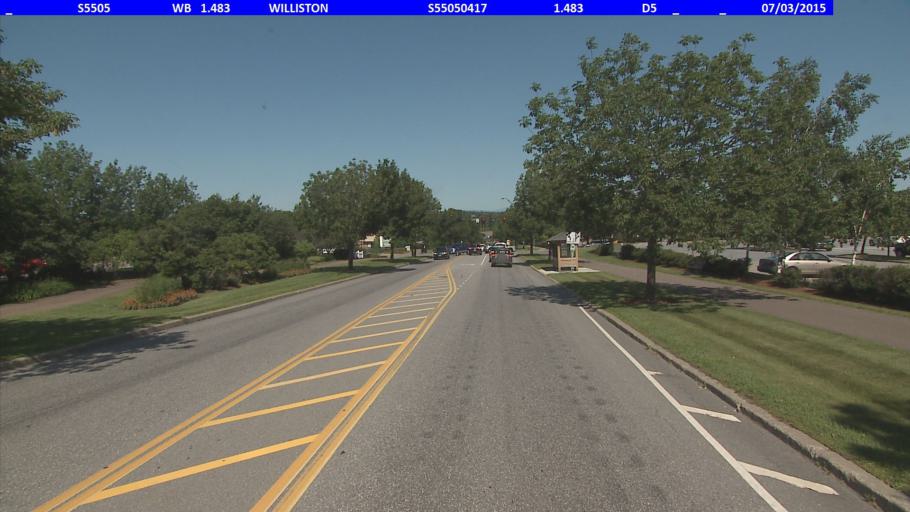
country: US
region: Vermont
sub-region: Chittenden County
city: Essex Junction
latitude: 44.4447
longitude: -73.1140
